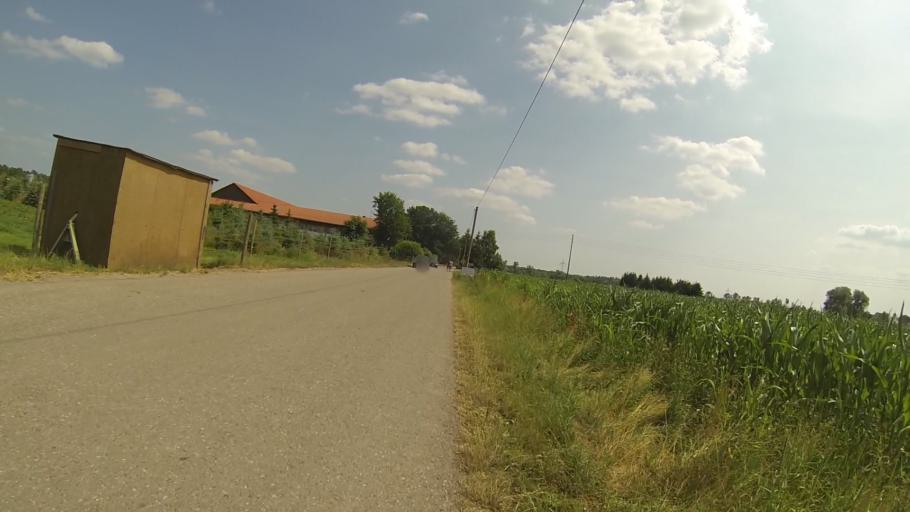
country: DE
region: Bavaria
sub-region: Swabia
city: Guenzburg
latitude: 48.4856
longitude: 10.2875
